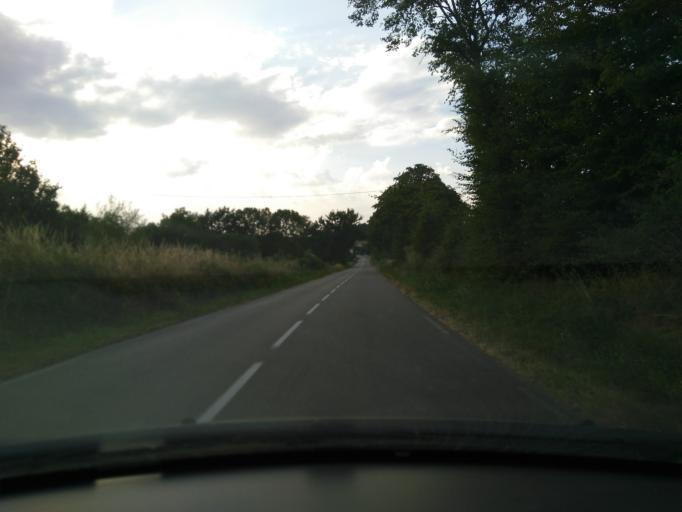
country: FR
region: Rhone-Alpes
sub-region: Departement de l'Isere
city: Beaurepaire
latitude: 45.4002
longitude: 5.1328
